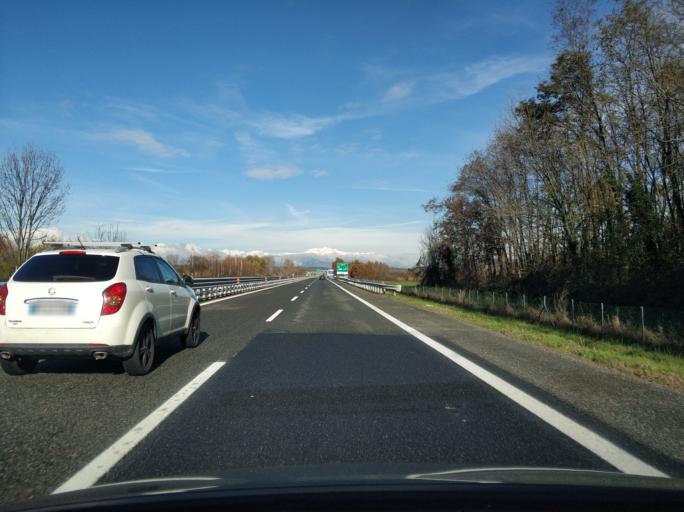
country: IT
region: Piedmont
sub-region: Provincia di Torino
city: San Giusto Canavese
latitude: 45.3072
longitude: 7.8184
